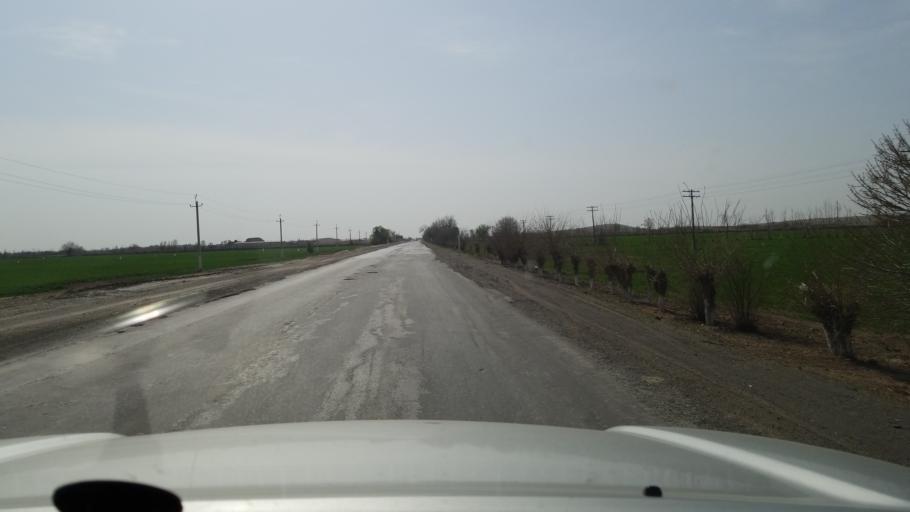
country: TM
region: Lebap
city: Sayat
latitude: 38.8436
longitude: 63.8138
